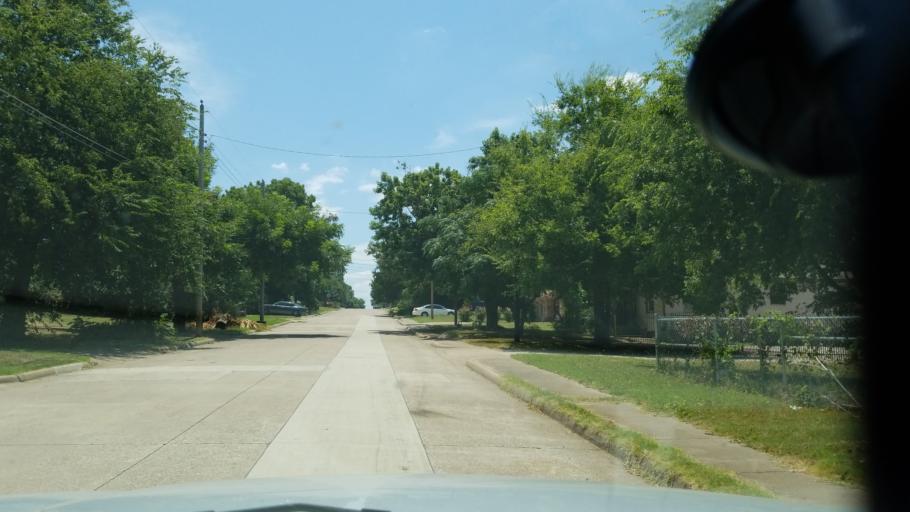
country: US
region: Texas
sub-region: Dallas County
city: Grand Prairie
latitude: 32.7593
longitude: -96.9615
